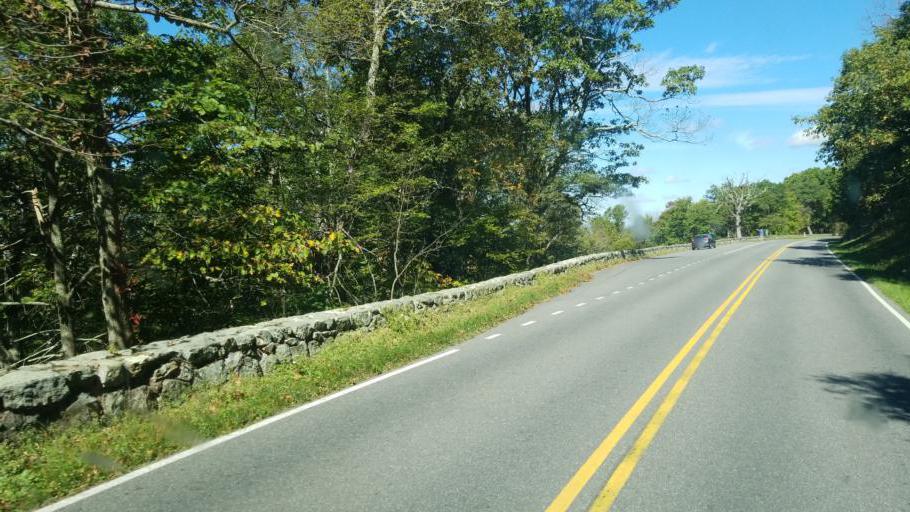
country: US
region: Virginia
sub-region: Greene County
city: Stanardsville
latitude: 38.4192
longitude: -78.4883
